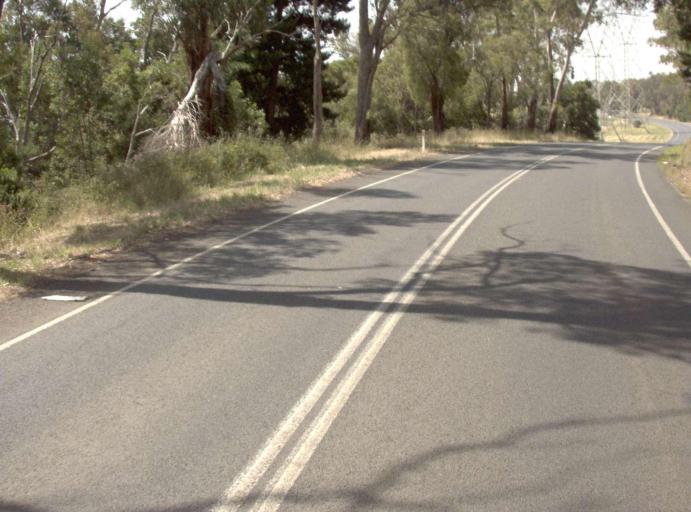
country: AU
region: Victoria
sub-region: Latrobe
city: Traralgon
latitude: -38.2573
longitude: 146.5484
